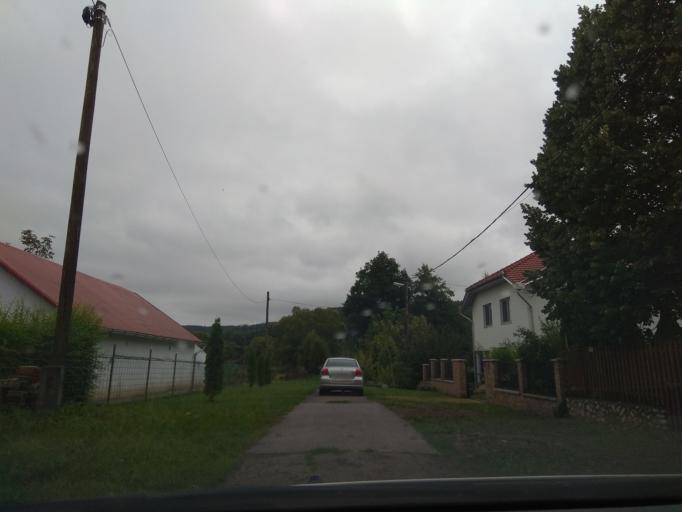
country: HU
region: Borsod-Abauj-Zemplen
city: Harsany
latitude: 47.9930
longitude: 20.7641
